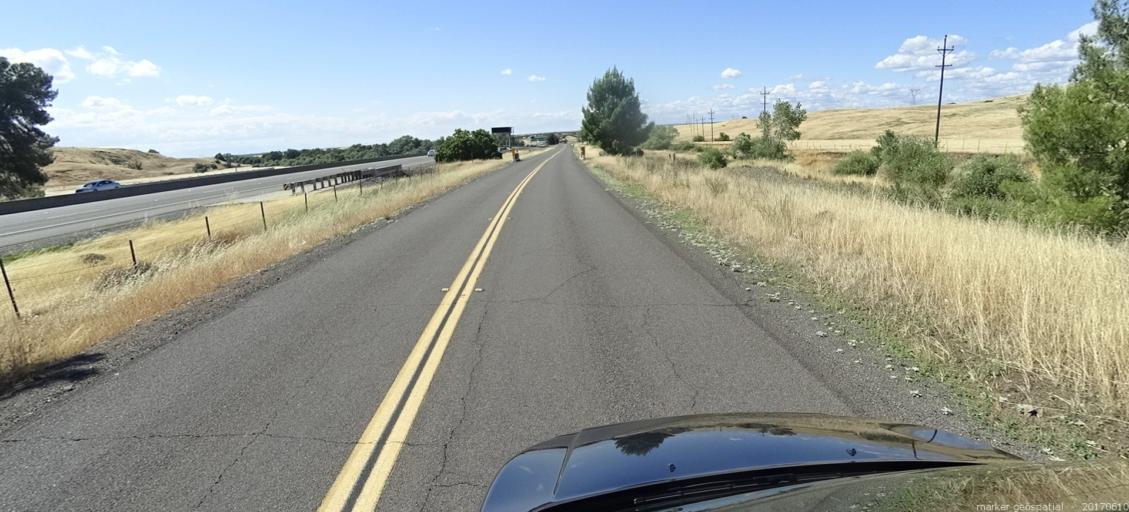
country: US
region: California
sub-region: Butte County
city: Thermalito
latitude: 39.5707
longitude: -121.6124
